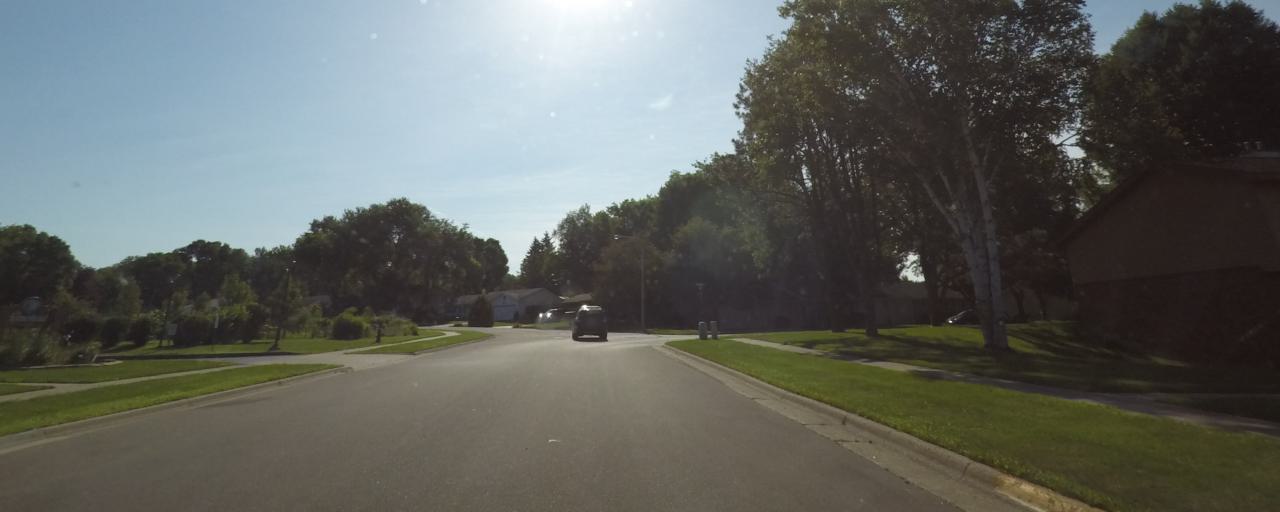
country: US
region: Wisconsin
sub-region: Dane County
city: McFarland
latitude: 43.0138
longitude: -89.2864
